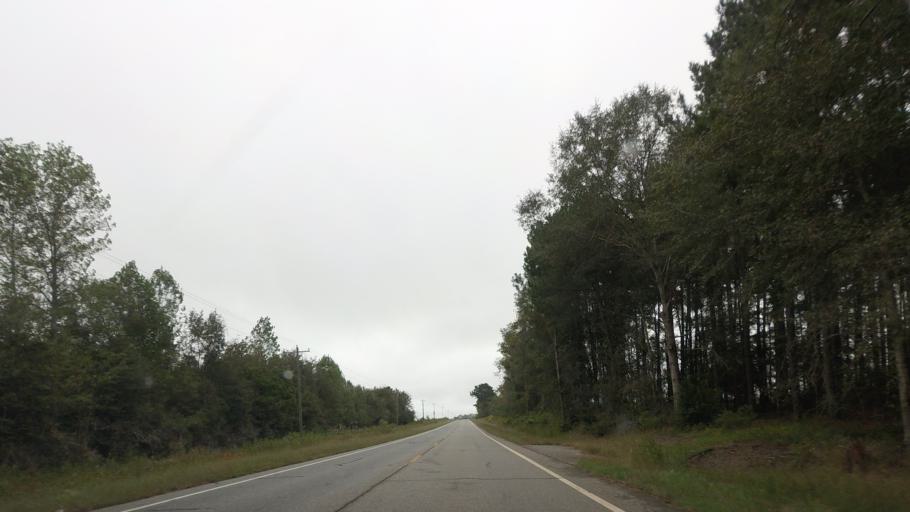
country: US
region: Georgia
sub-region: Irwin County
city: Ocilla
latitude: 31.5154
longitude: -83.2410
